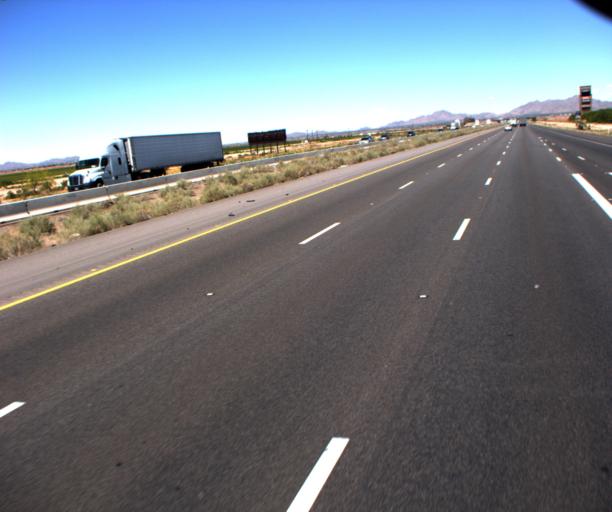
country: US
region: Arizona
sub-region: Pinal County
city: Casa Grande
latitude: 32.8833
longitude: -111.6867
